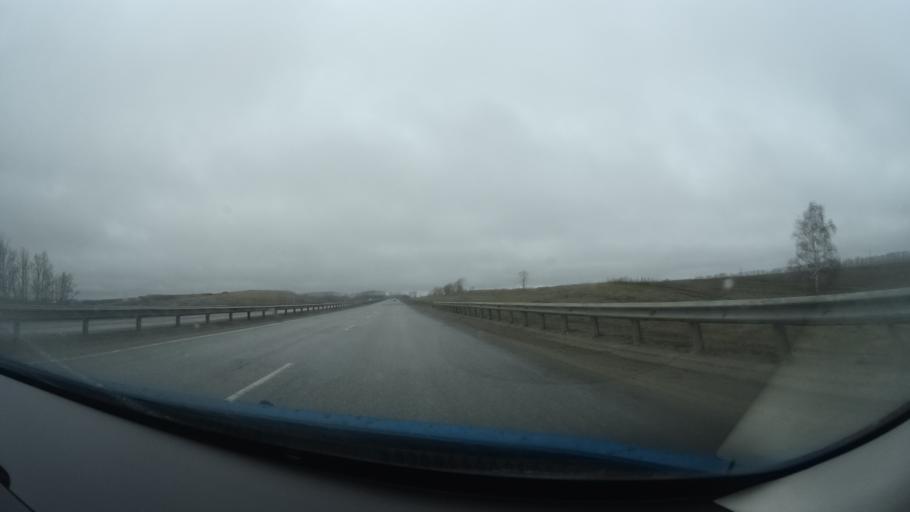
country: RU
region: Bashkortostan
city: Alekseyevka
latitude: 54.7379
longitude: 55.1087
